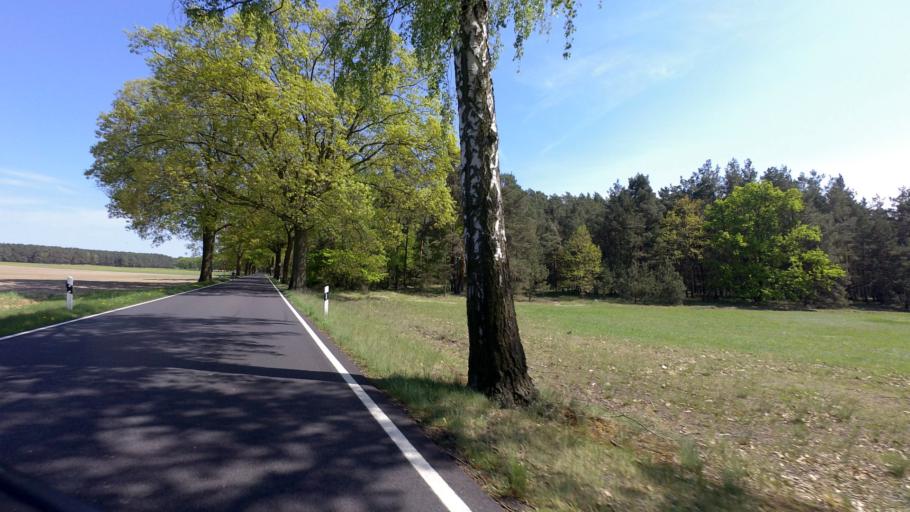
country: DE
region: Brandenburg
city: Neu Zauche
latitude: 51.9979
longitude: 14.1269
